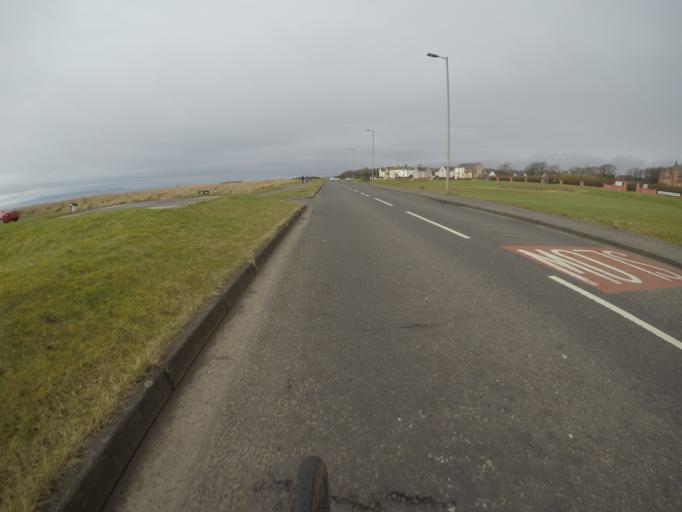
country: GB
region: Scotland
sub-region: North Ayrshire
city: Ardrossan
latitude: 55.6505
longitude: -4.8174
